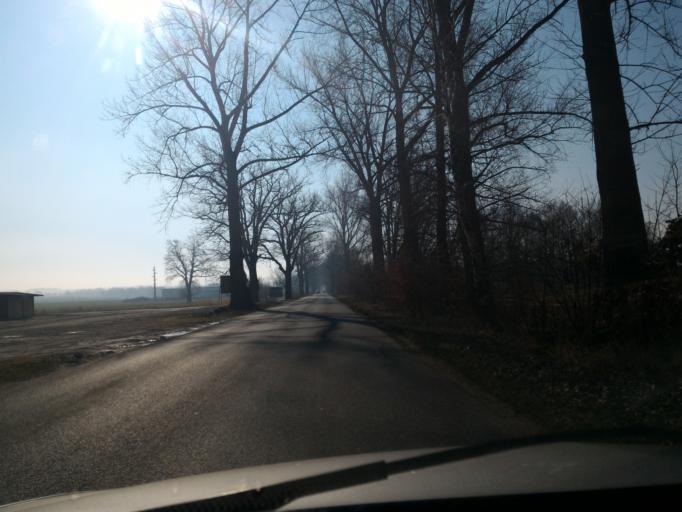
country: DE
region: Saxony
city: Zittau
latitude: 50.8795
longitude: 14.8226
